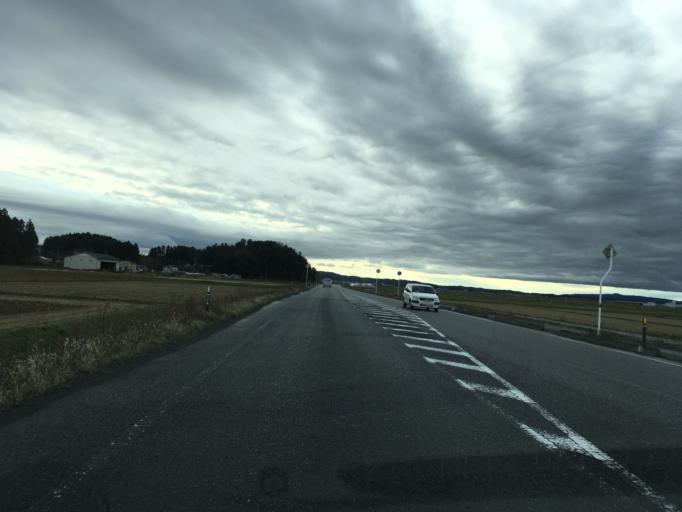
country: JP
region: Miyagi
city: Wakuya
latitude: 38.6991
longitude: 141.2603
